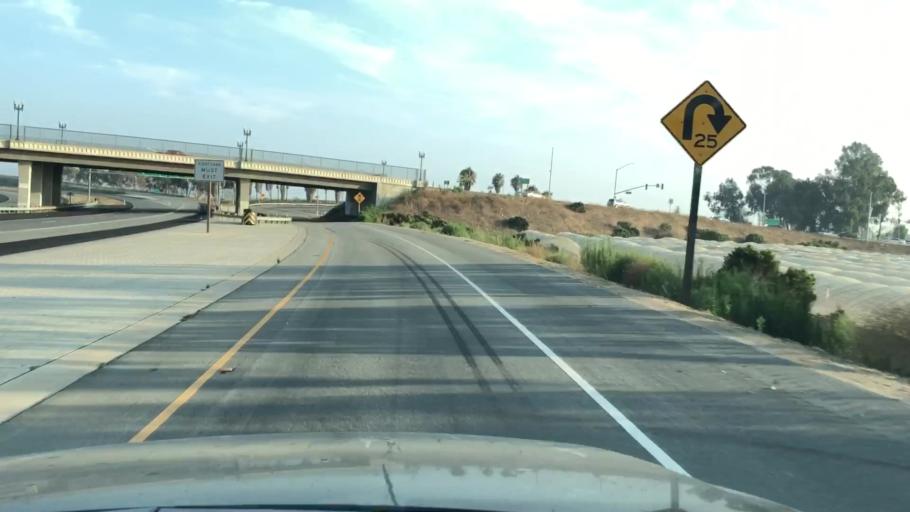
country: US
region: California
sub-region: Ventura County
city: Oxnard
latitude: 34.1675
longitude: -119.1430
